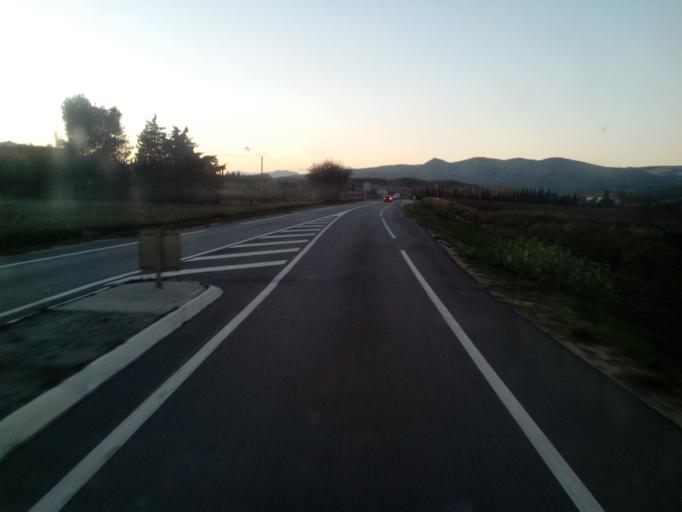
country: FR
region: Languedoc-Roussillon
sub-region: Departement des Pyrenees-Orientales
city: Peyrestortes
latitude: 42.7681
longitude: 2.8389
